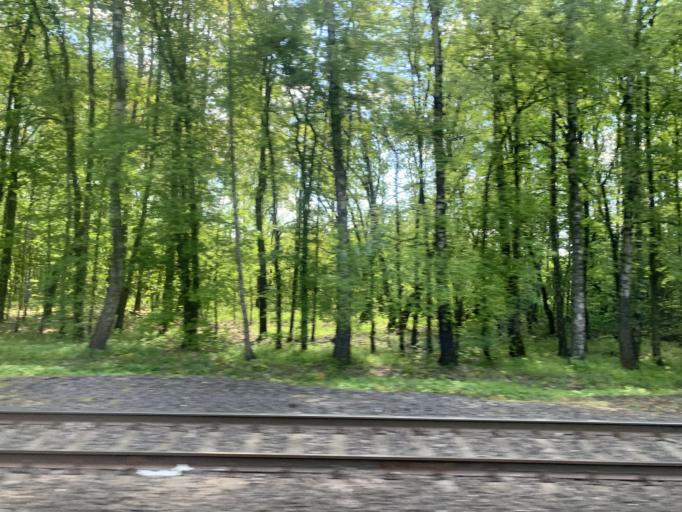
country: BY
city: Fanipol
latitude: 53.7538
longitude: 27.3559
